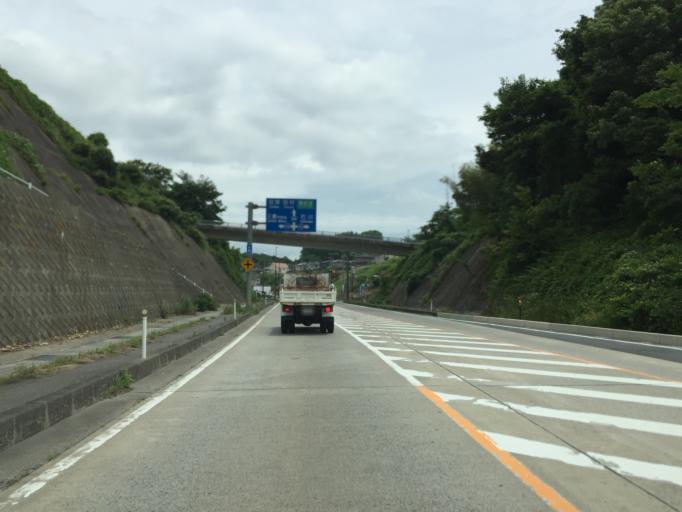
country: JP
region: Fukushima
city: Miharu
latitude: 37.4328
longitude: 140.4943
